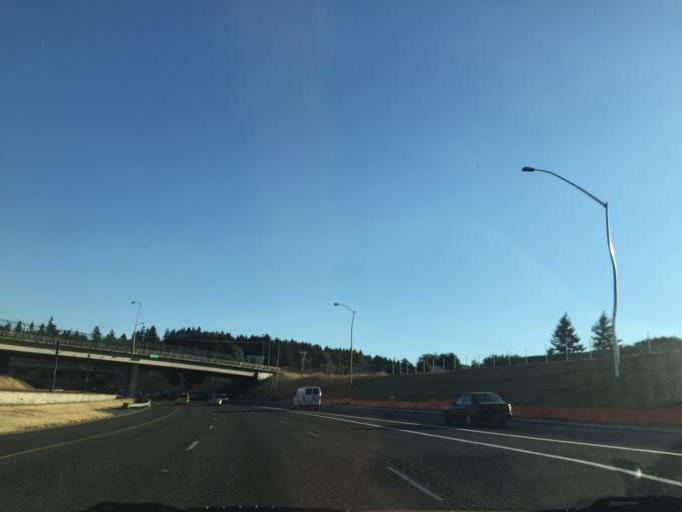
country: US
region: Oregon
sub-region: Multnomah County
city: Lents
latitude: 45.5587
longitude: -122.5664
